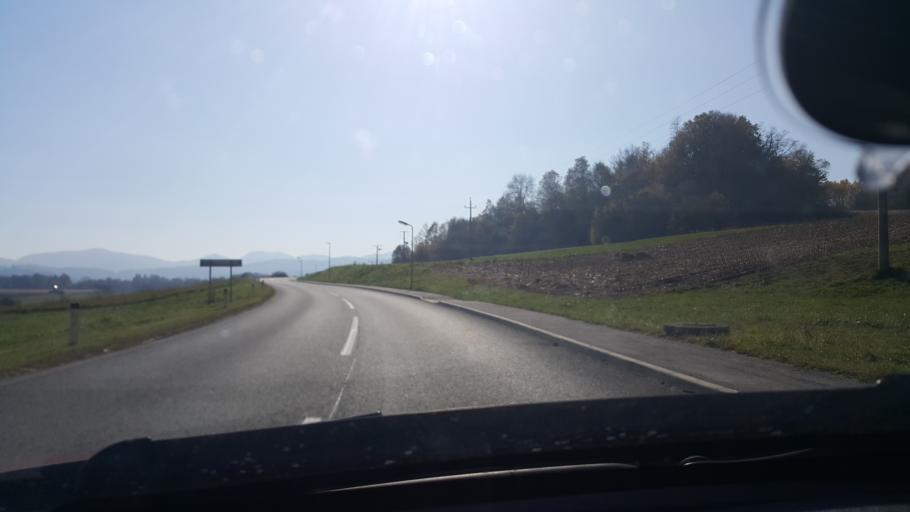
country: SI
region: Podcetrtek
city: Podcetrtek
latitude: 46.1267
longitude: 15.5995
